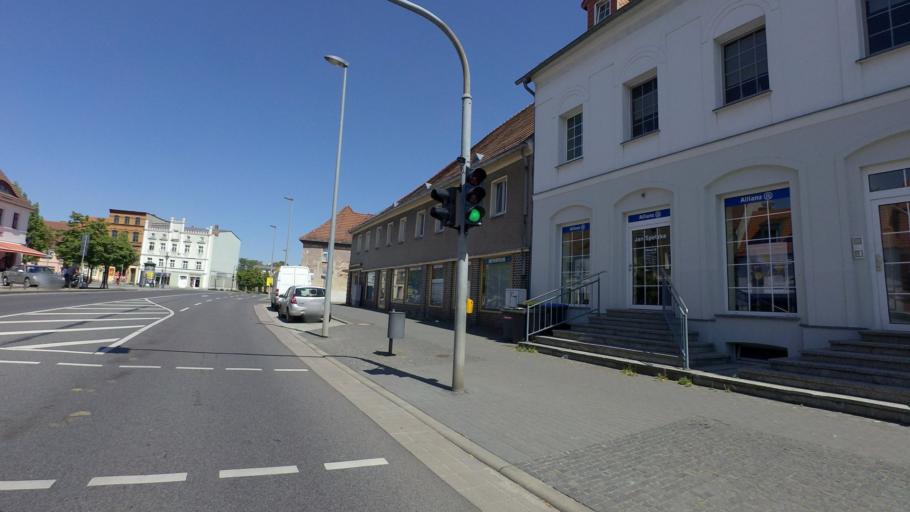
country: DE
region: Brandenburg
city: Peitz
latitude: 51.8577
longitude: 14.4113
